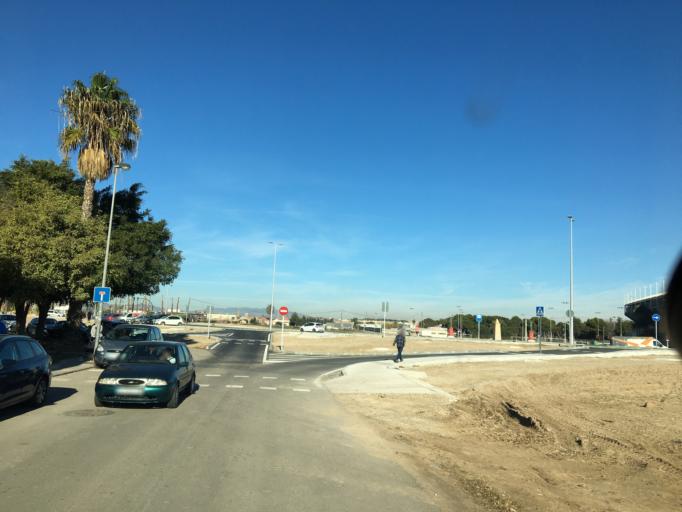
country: ES
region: Murcia
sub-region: Murcia
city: Cartagena
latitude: 37.6078
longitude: -0.9965
